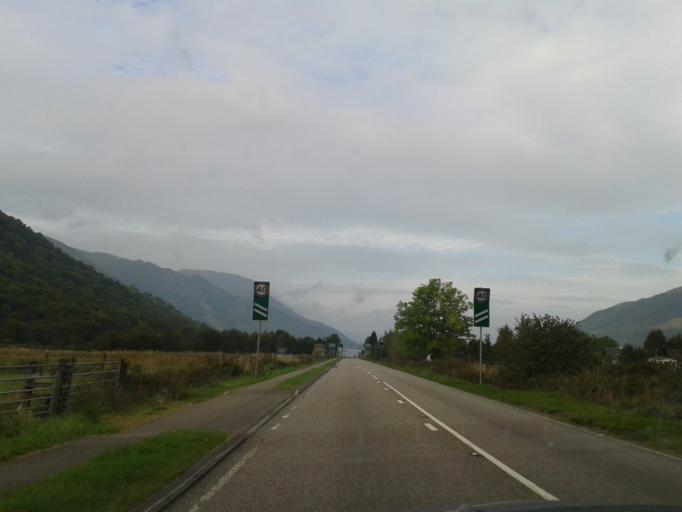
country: GB
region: Scotland
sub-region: Highland
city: Fort William
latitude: 56.6812
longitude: -5.0983
